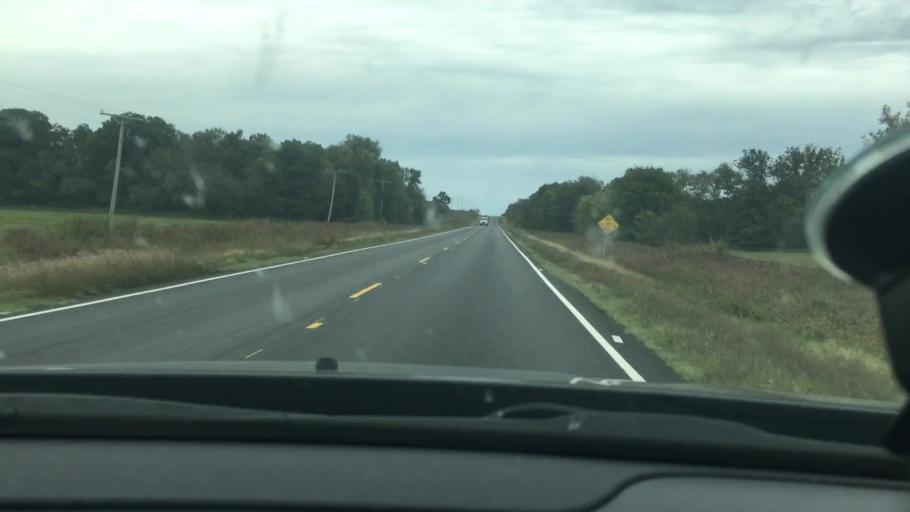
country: US
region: Oklahoma
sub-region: Coal County
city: Coalgate
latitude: 34.4037
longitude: -96.4245
